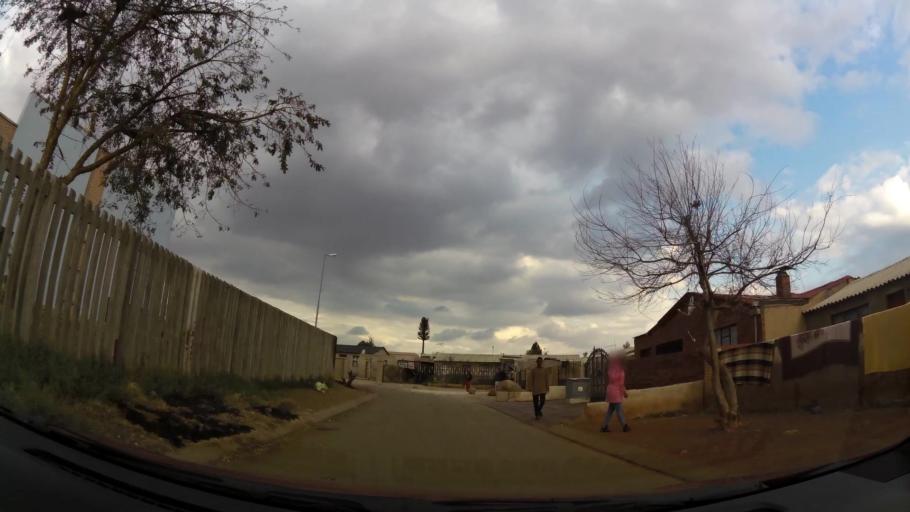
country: ZA
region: Gauteng
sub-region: City of Johannesburg Metropolitan Municipality
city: Soweto
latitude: -26.2398
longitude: 27.8225
